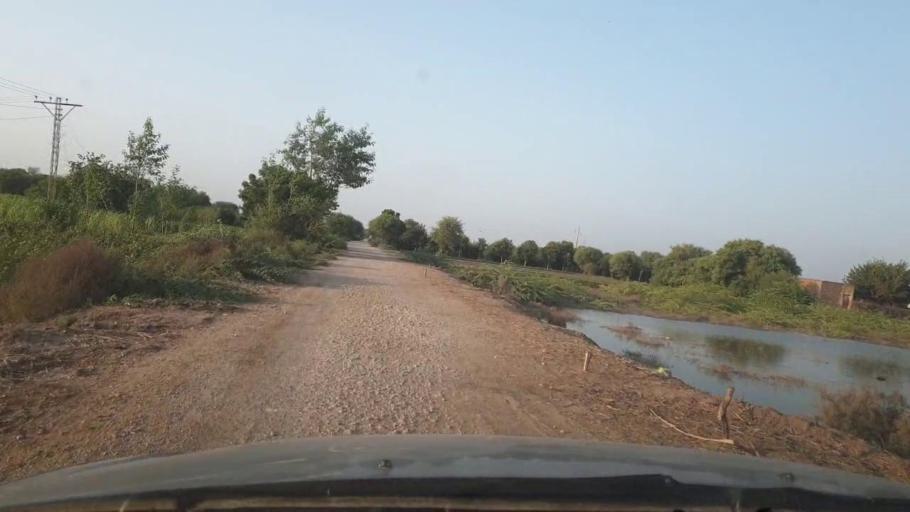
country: PK
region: Sindh
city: Tando Ghulam Ali
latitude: 25.1557
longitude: 68.9747
